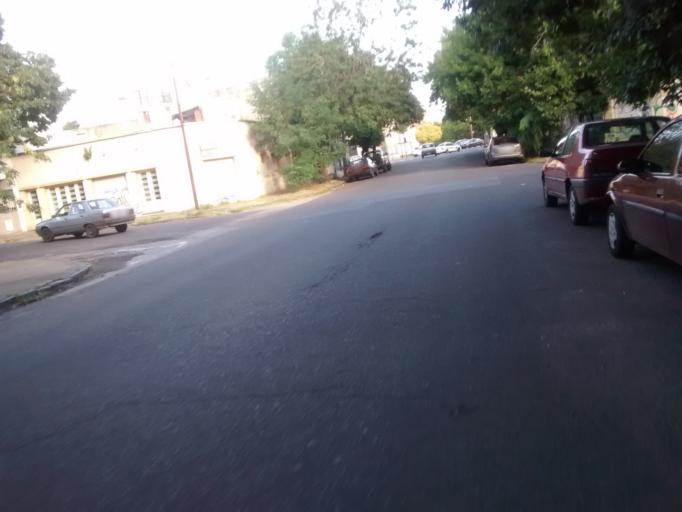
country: AR
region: Buenos Aires
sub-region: Partido de La Plata
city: La Plata
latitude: -34.9262
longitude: -57.9551
